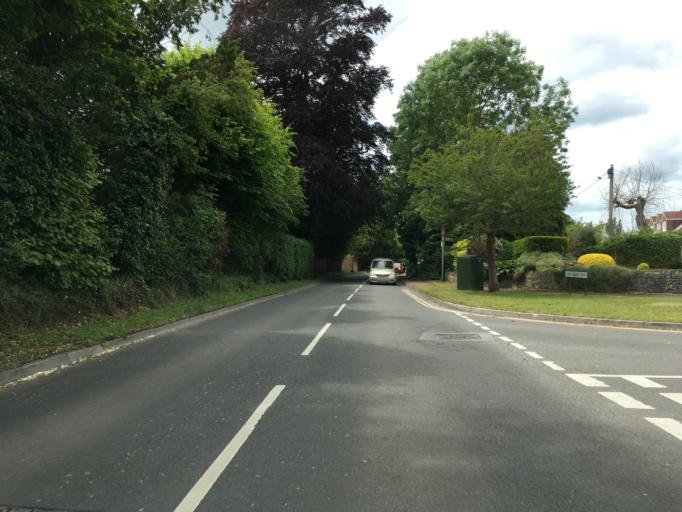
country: GB
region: England
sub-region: Wiltshire
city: Purton
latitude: 51.5729
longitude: -1.8719
